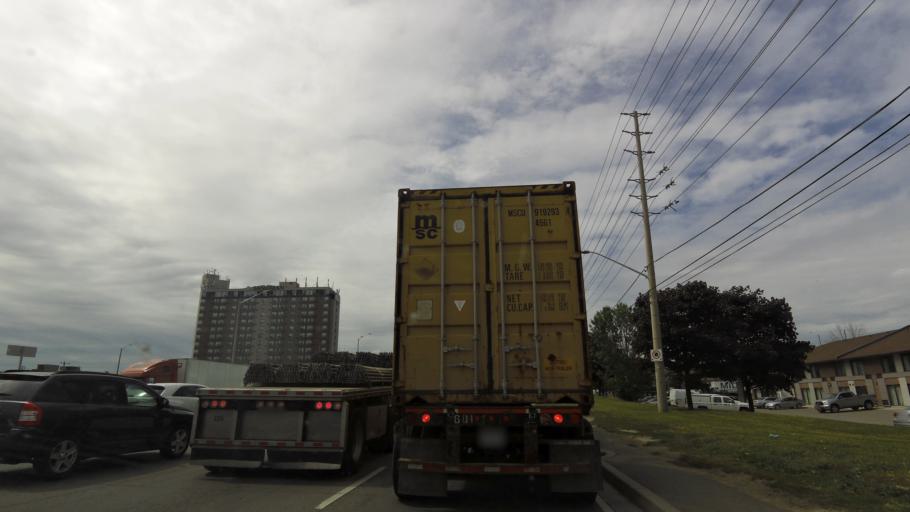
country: CA
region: Ontario
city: Etobicoke
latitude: 43.6419
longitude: -79.6290
